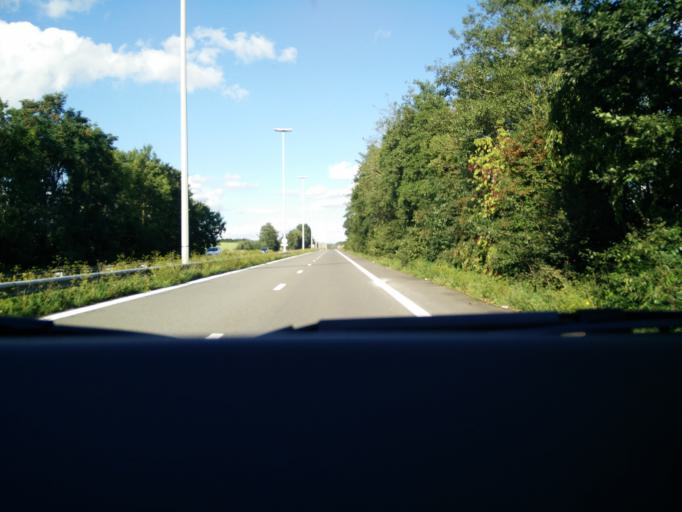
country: BE
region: Wallonia
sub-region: Province du Hainaut
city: Erquelinnes
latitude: 50.3164
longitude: 4.1049
